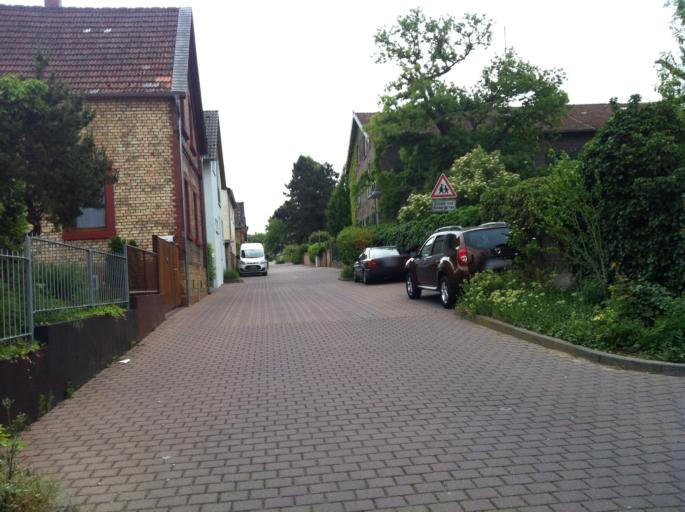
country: DE
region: Rheinland-Pfalz
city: Budenheim
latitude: 50.0239
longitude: 8.1750
